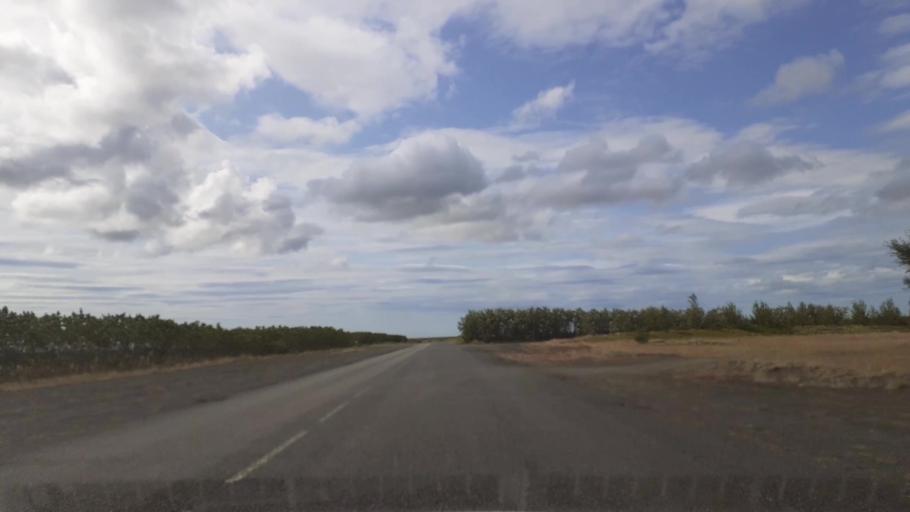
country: IS
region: South
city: Vestmannaeyjar
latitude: 63.8301
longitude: -20.4001
